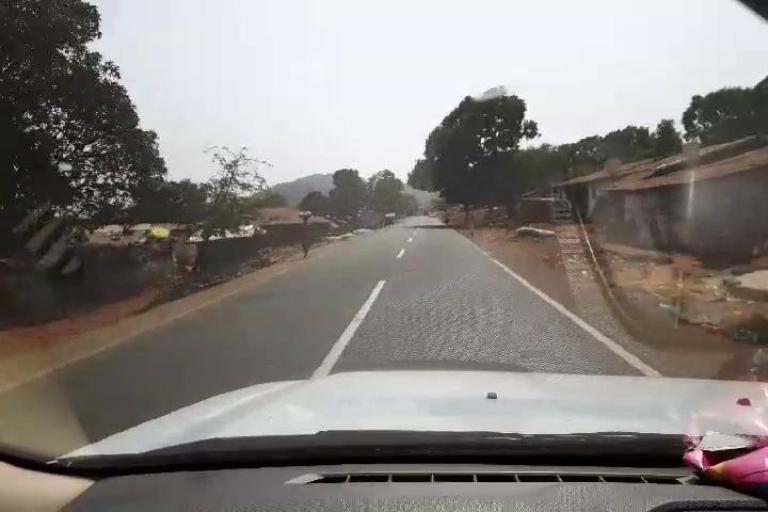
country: SL
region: Western Area
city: Waterloo
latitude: 8.2019
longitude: -13.1225
